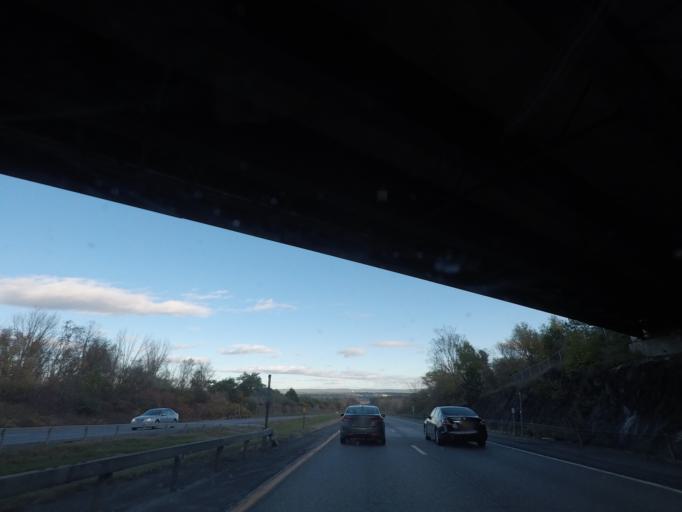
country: US
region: New York
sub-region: Albany County
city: Cohoes
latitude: 42.7571
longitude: -73.7365
